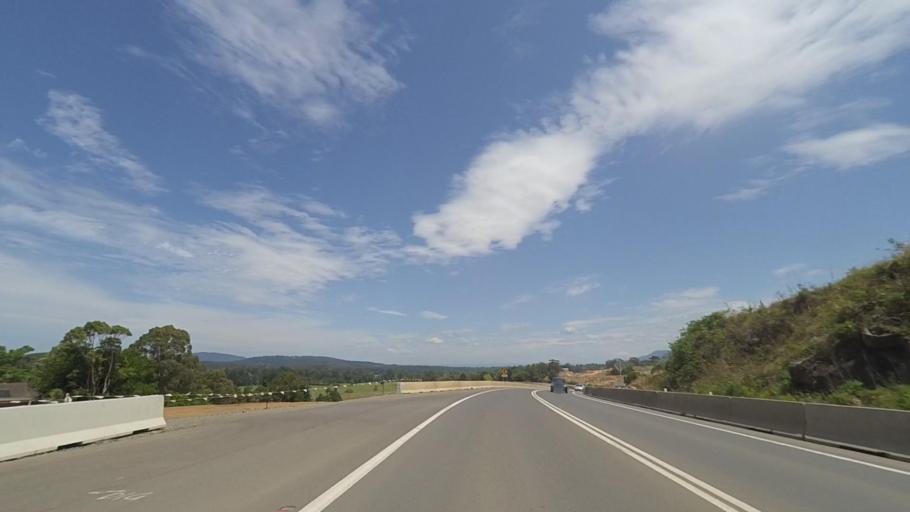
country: AU
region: New South Wales
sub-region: Shoalhaven Shire
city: Berry
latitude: -34.7581
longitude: 150.7440
